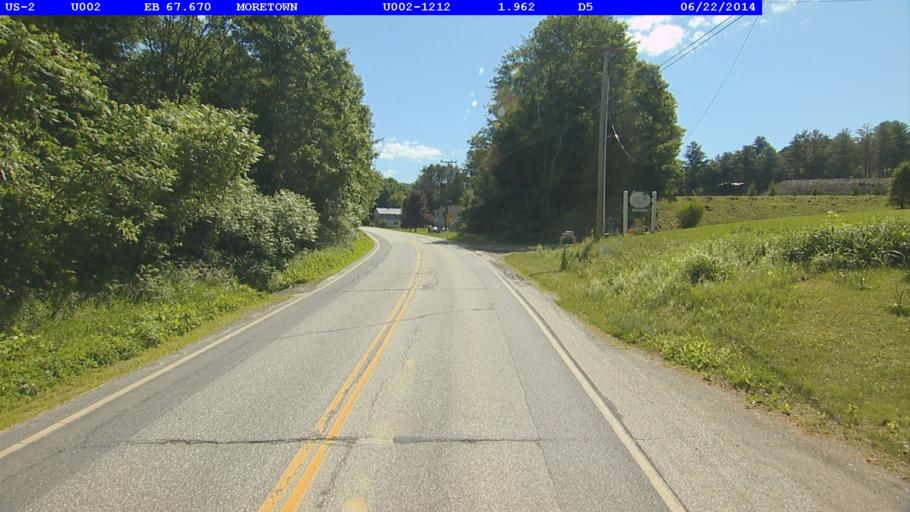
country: US
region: Vermont
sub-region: Washington County
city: Waterbury
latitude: 44.3113
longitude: -72.7153
